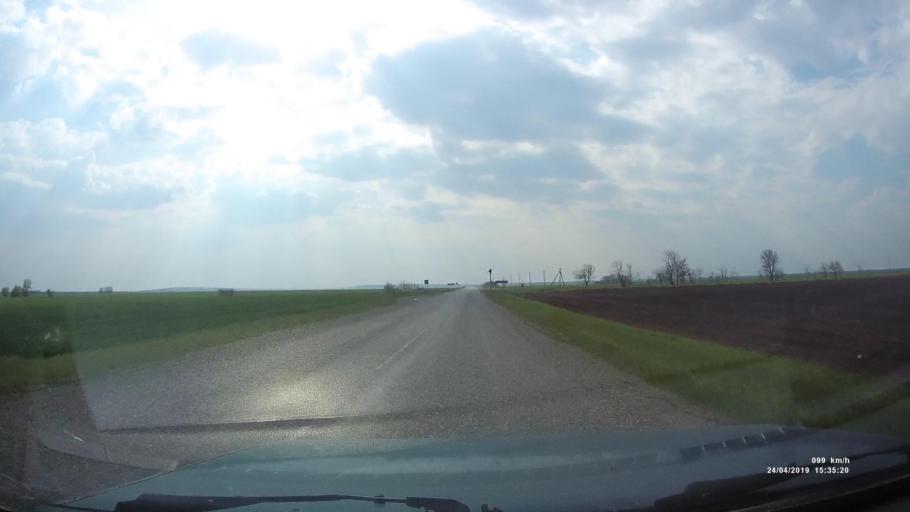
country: RU
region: Kalmykiya
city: Yashalta
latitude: 46.5994
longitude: 42.8962
